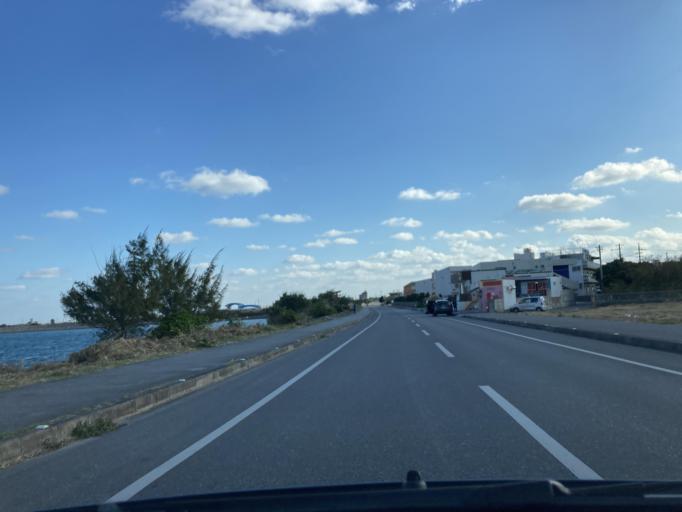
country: JP
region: Okinawa
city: Katsuren-haebaru
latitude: 26.3136
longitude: 127.9190
